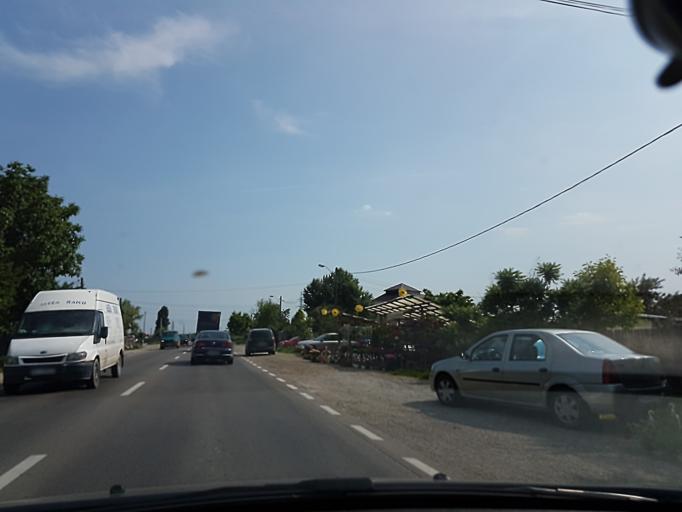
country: RO
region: Prahova
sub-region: Comuna Blejoiu
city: Blejoi
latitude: 45.0014
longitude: 26.0185
